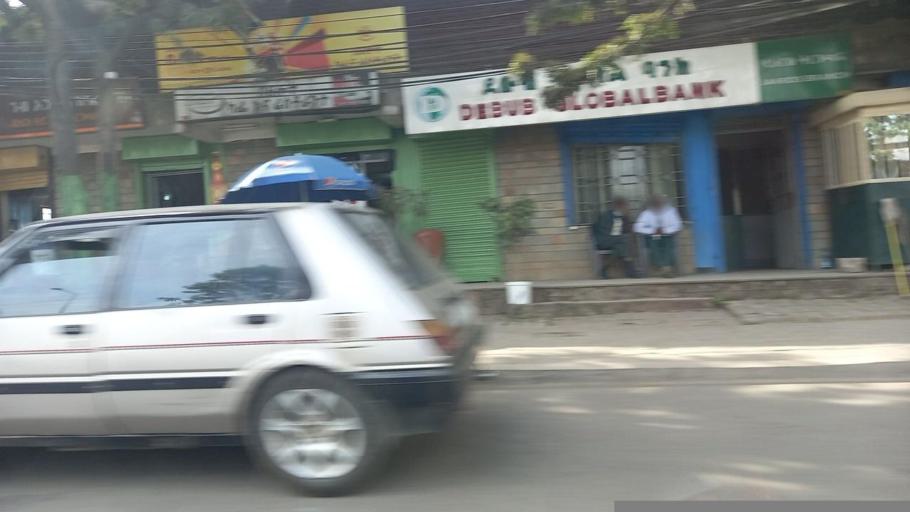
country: ET
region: Adis Abeba
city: Addis Ababa
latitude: 9.0083
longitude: 38.8200
